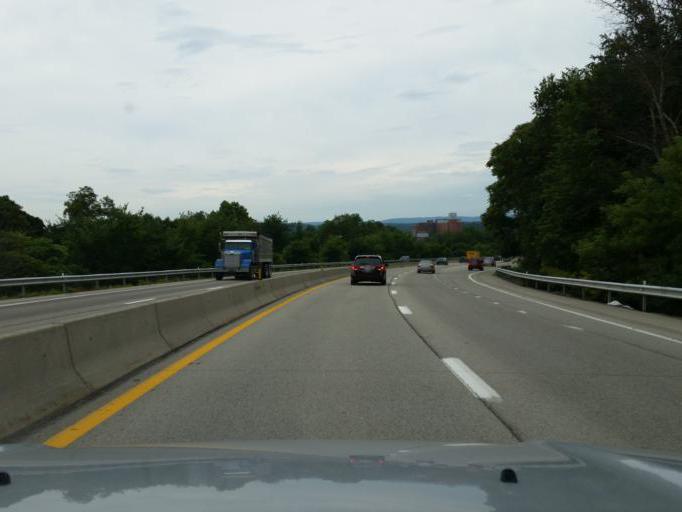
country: US
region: Pennsylvania
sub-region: Westmoreland County
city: Southwest Greensburg
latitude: 40.3073
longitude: -79.5670
